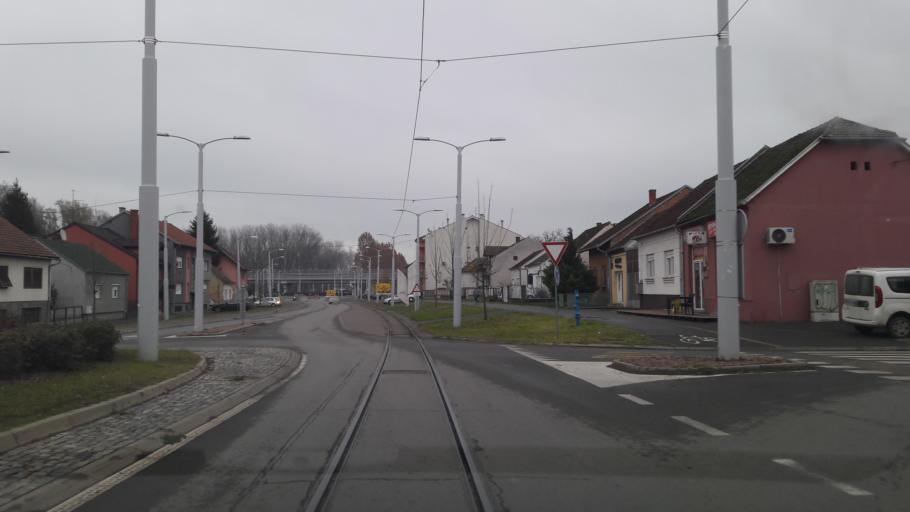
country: HR
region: Osjecko-Baranjska
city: Visnjevac
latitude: 45.5650
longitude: 18.6273
